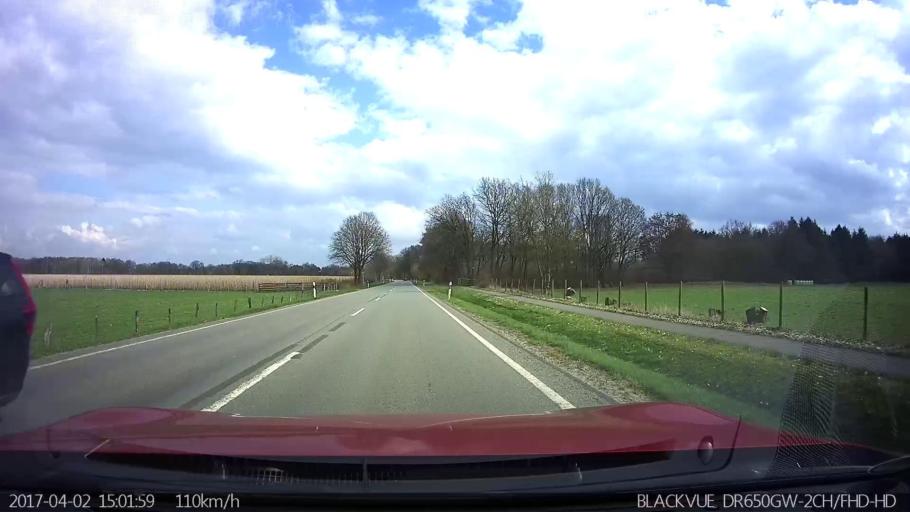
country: DE
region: Schleswig-Holstein
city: Appen
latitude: 53.6302
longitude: 9.7259
